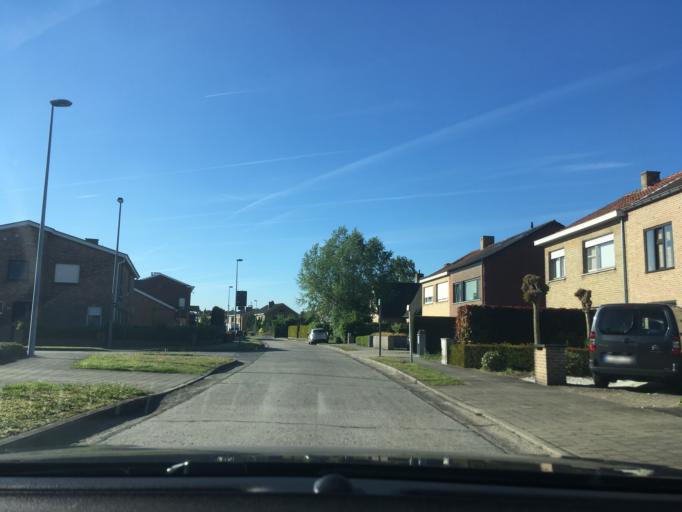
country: BE
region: Flanders
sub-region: Provincie West-Vlaanderen
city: Oostkamp
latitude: 51.1789
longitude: 3.2162
